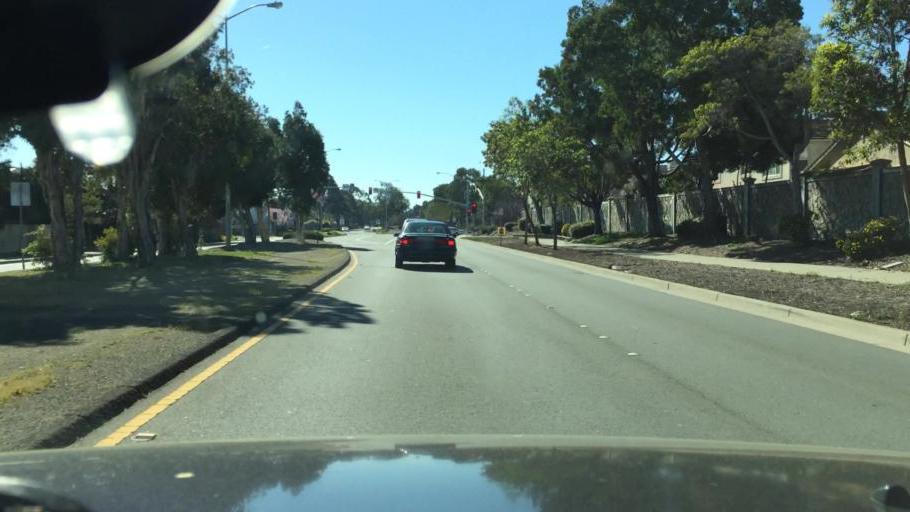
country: US
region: California
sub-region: Alameda County
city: Union City
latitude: 37.5826
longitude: -122.0810
